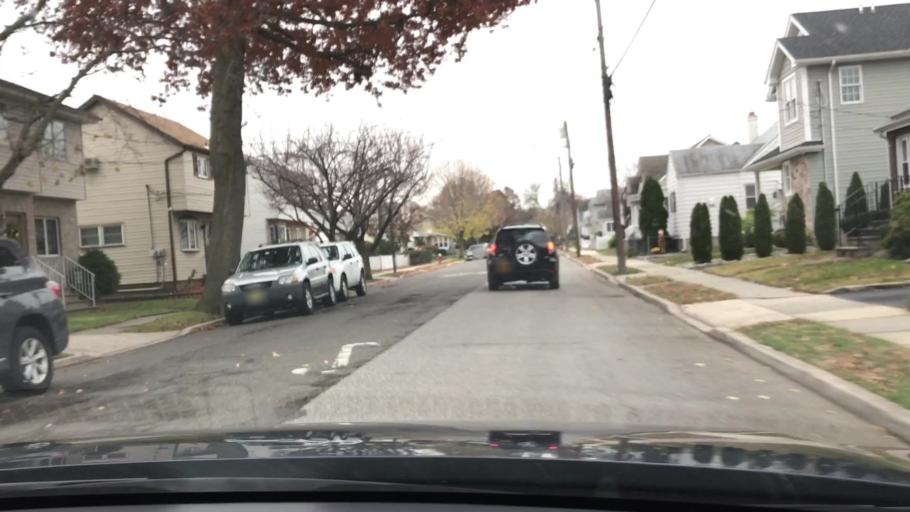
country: US
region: New Jersey
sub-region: Bergen County
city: Wallington
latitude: 40.8473
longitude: -74.1166
